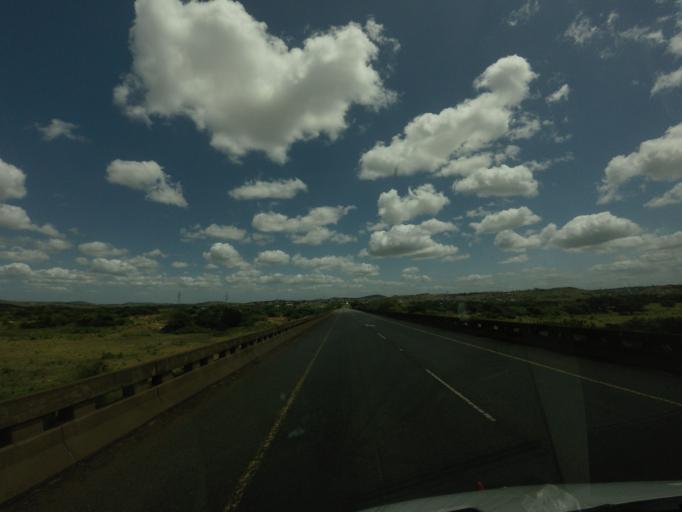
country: ZA
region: KwaZulu-Natal
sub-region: uMkhanyakude District Municipality
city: Mtubatuba
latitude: -28.4575
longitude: 32.1479
